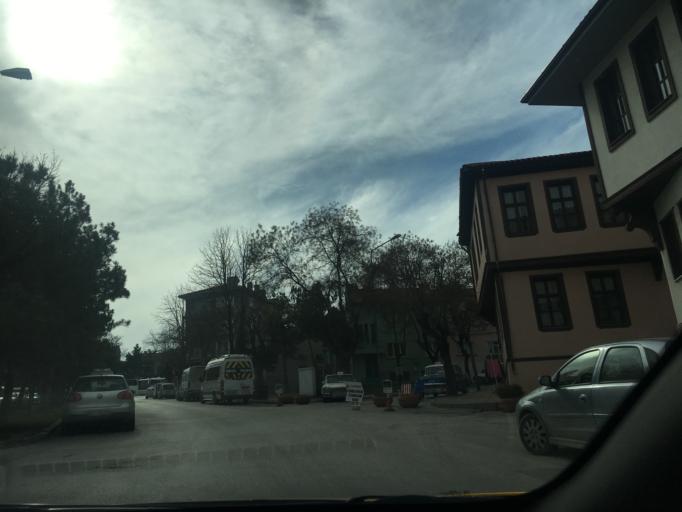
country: TR
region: Eskisehir
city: Eskisehir
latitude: 39.7634
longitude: 30.5245
